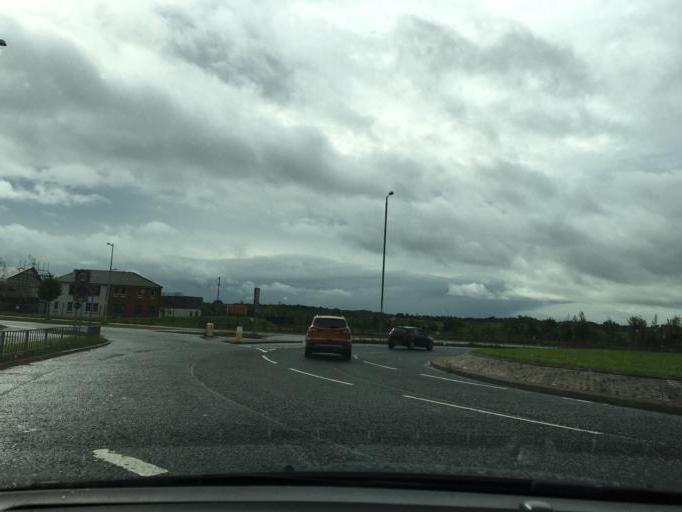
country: GB
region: Scotland
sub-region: North Lanarkshire
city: Holytown
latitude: 55.7965
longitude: -3.9600
